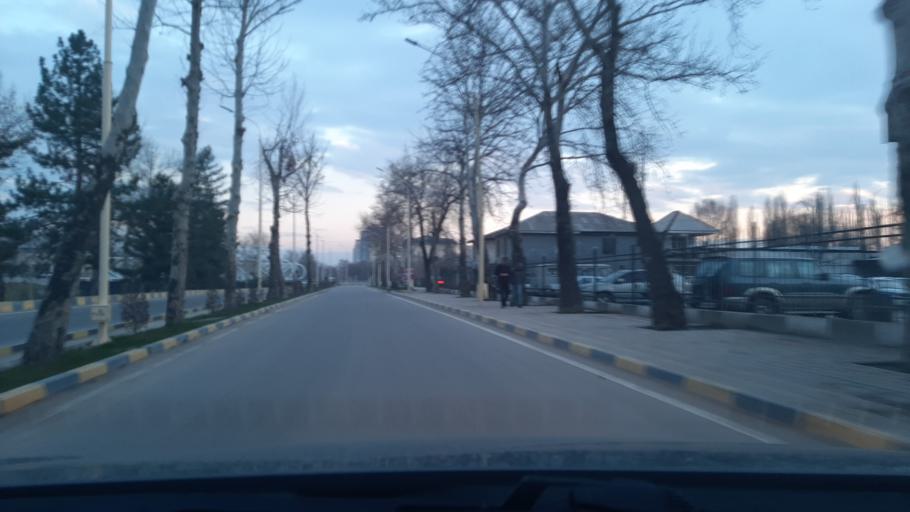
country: TJ
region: Dushanbe
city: Dushanbe
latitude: 38.5712
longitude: 68.7542
